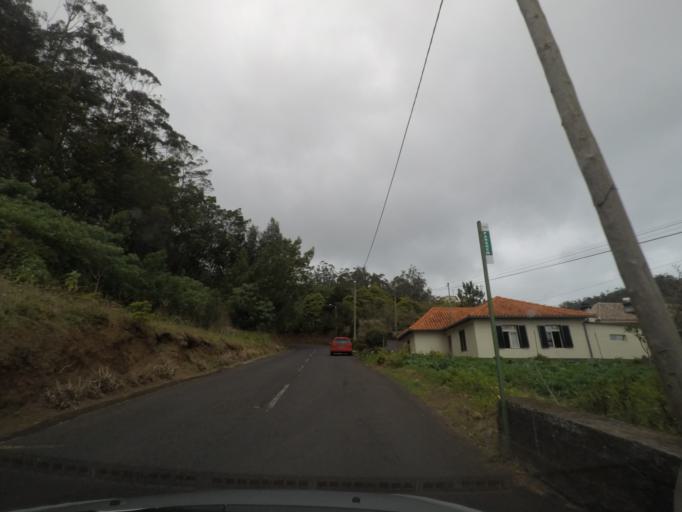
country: PT
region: Madeira
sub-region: Santa Cruz
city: Santa Cruz
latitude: 32.7393
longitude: -16.8231
